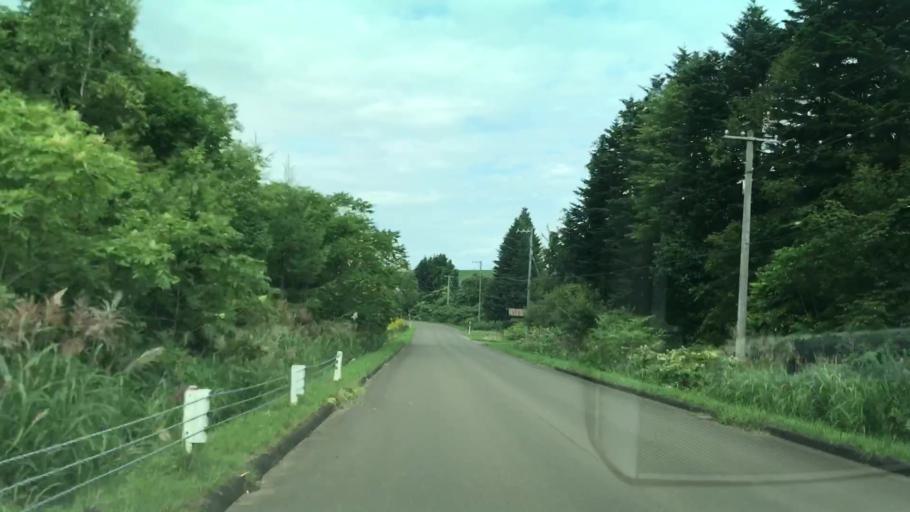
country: JP
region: Hokkaido
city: Yoichi
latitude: 43.1723
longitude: 140.8289
